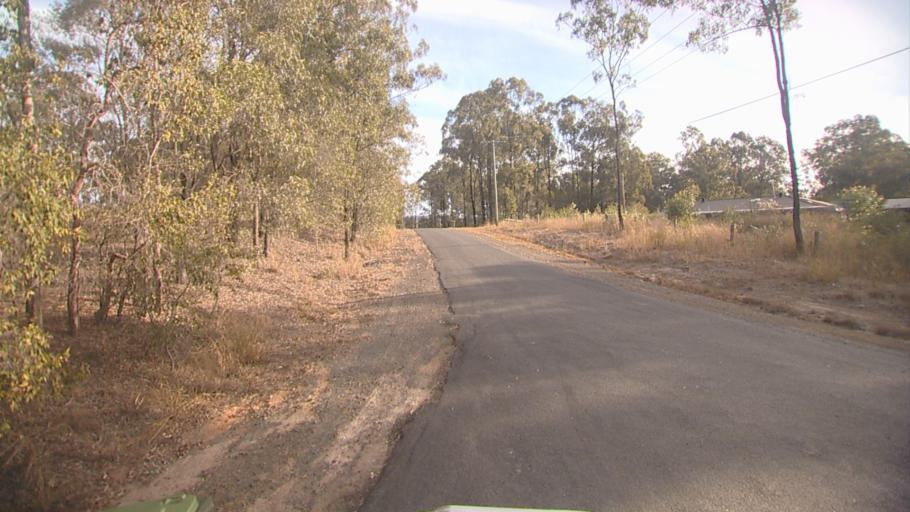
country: AU
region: Queensland
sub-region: Logan
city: Cedar Vale
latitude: -27.8744
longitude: 153.0279
